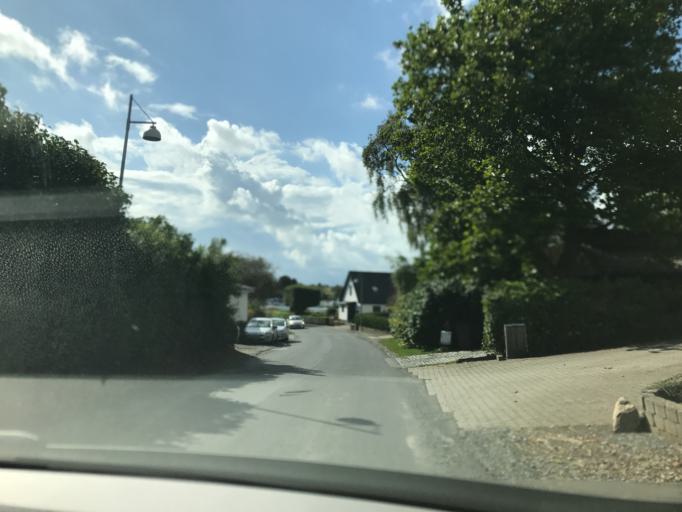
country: DK
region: South Denmark
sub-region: Middelfart Kommune
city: Norre Aby
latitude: 55.4616
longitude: 9.7991
